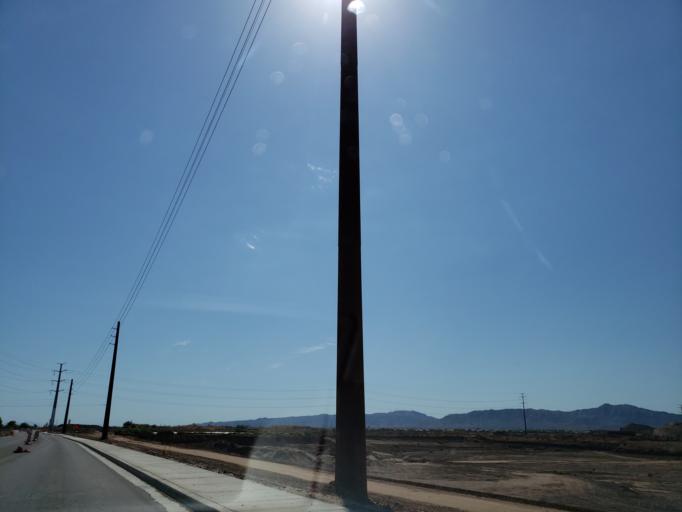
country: US
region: Arizona
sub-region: Maricopa County
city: Laveen
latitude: 33.4080
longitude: -112.1899
